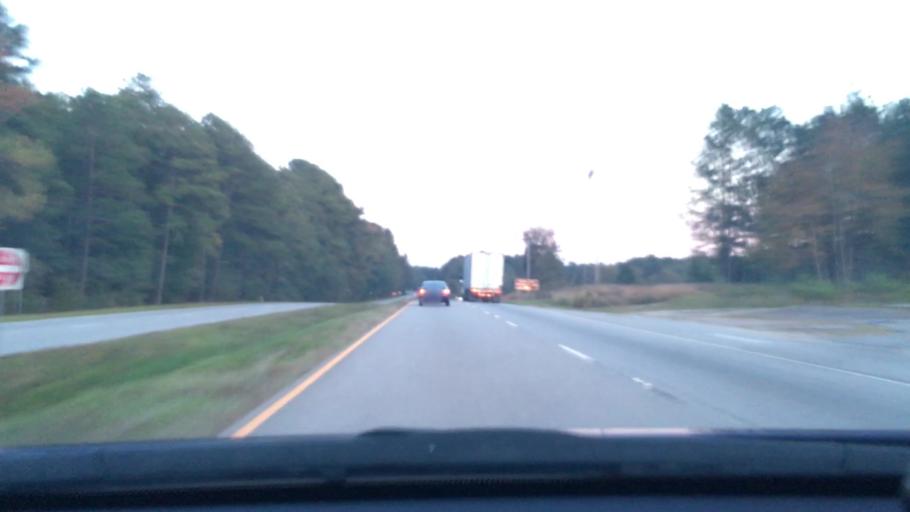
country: US
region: South Carolina
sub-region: Sumter County
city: Stateburg
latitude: 33.9435
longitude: -80.6588
